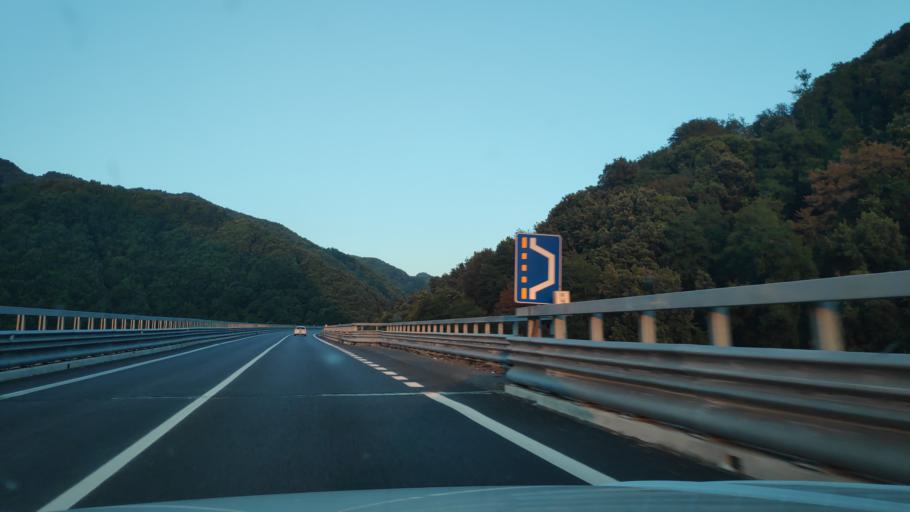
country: IT
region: Calabria
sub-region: Provincia di Reggio Calabria
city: Giffone
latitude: 38.4137
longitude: 16.1338
